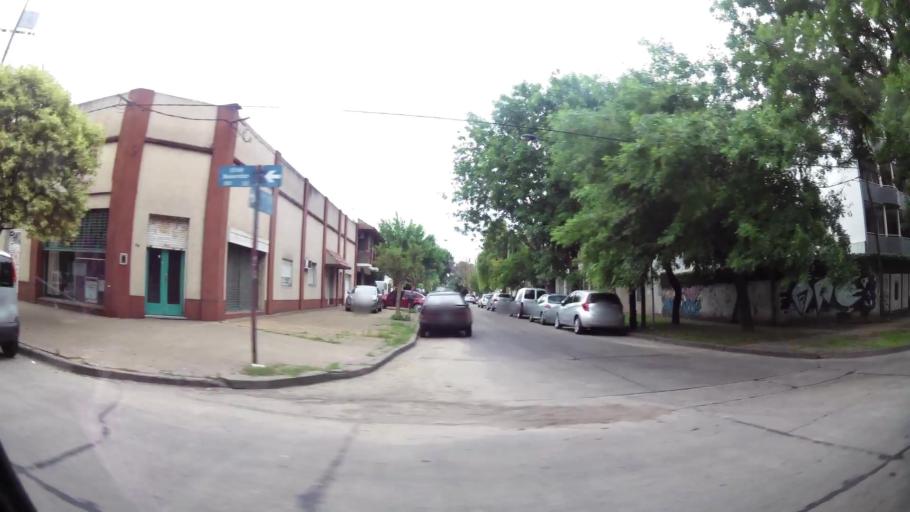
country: AR
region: Buenos Aires
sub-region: Partido de La Plata
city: La Plata
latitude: -34.9270
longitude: -57.9737
